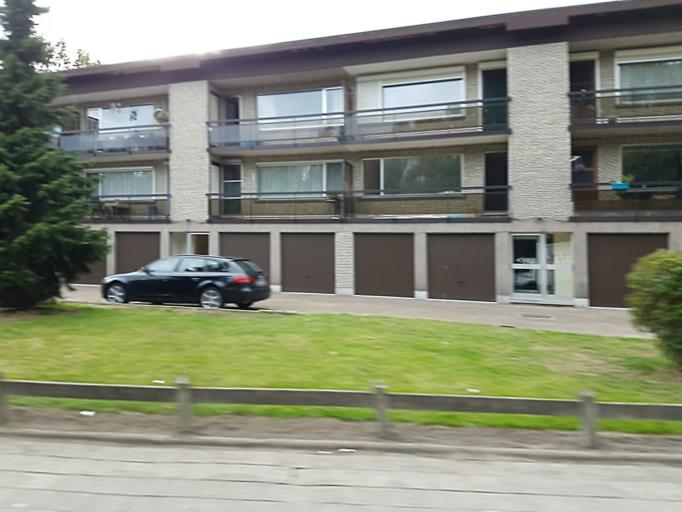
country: BE
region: Flanders
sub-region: Provincie Antwerpen
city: Zwijndrecht
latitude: 51.2082
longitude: 4.3502
